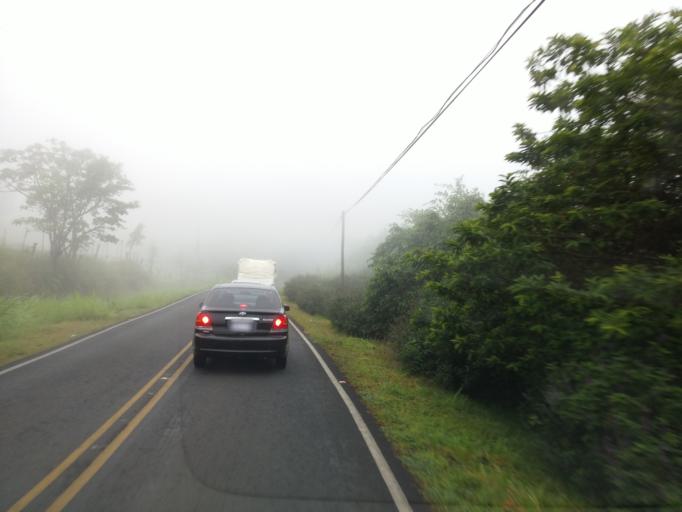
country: CR
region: Alajuela
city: San Ramon
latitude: 10.1801
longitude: -84.5041
